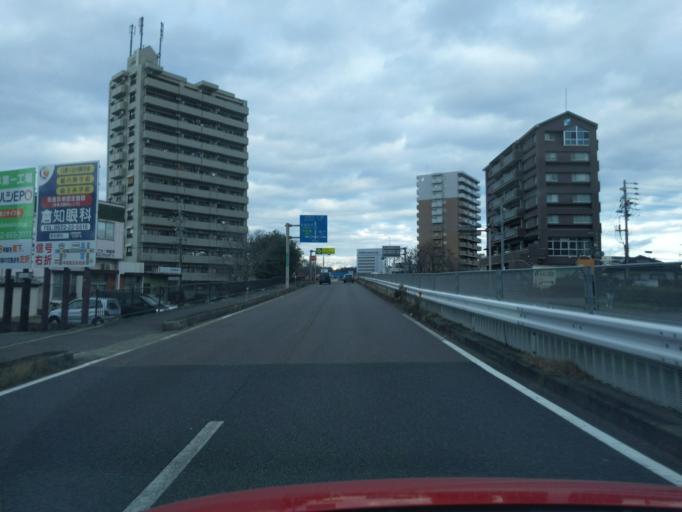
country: JP
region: Gifu
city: Tajimi
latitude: 35.3363
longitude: 137.1128
